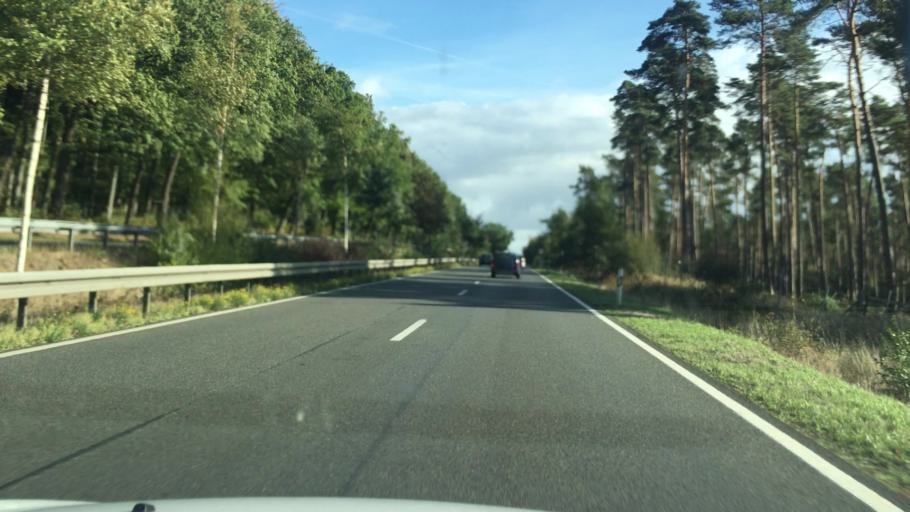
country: DE
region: Lower Saxony
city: Linsburg
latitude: 52.5723
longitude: 9.3092
